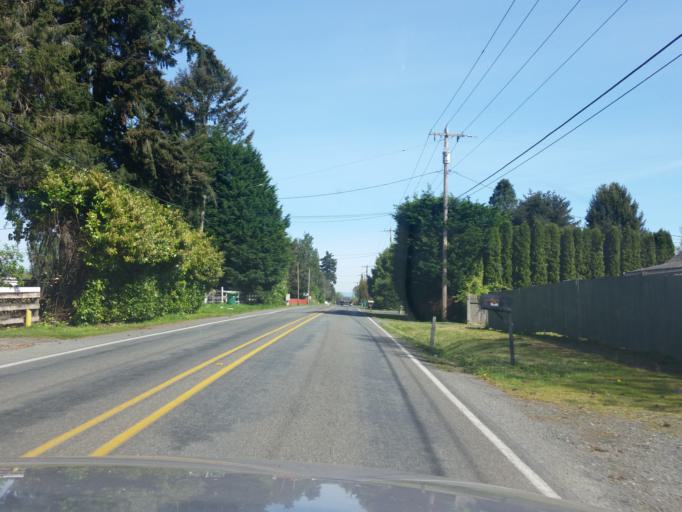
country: US
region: Washington
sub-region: Snohomish County
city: Cathcart
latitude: 47.8568
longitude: -122.0992
